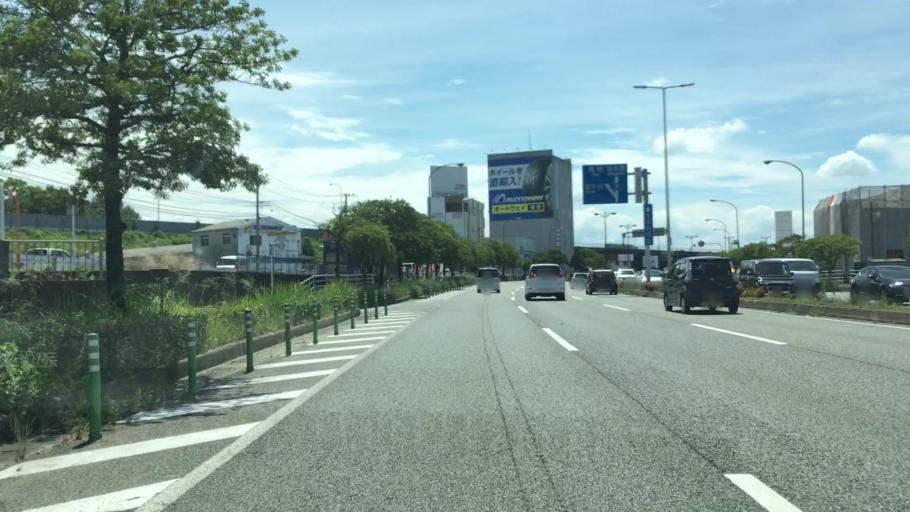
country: JP
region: Fukuoka
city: Onojo
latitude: 33.5283
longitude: 130.4944
